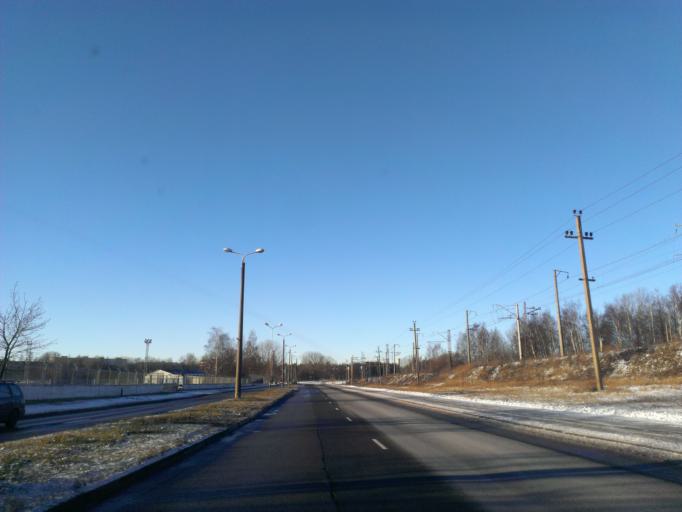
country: LV
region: Riga
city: Jaunciems
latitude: 57.0341
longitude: 24.1244
